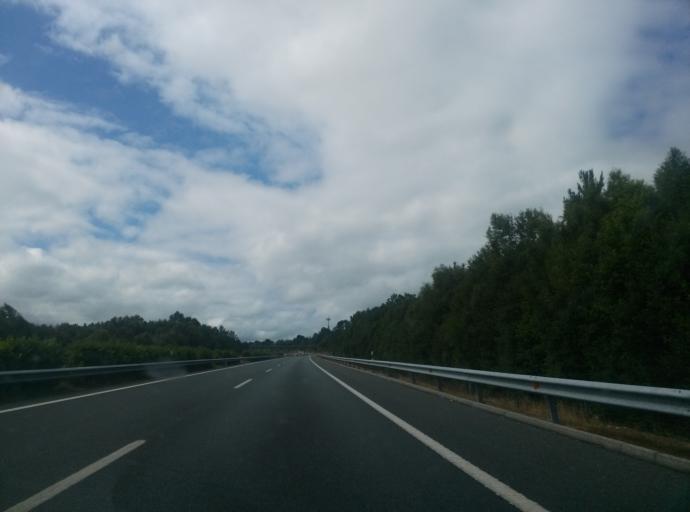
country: ES
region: Galicia
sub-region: Provincia de Lugo
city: Begonte
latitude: 43.1451
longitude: -7.6531
